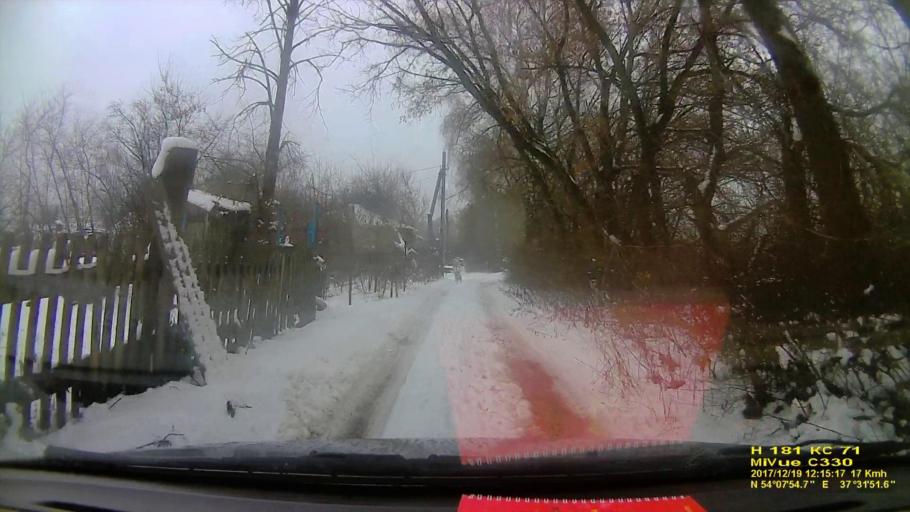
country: RU
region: Tula
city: Kosaya Gora
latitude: 54.1318
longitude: 37.5309
